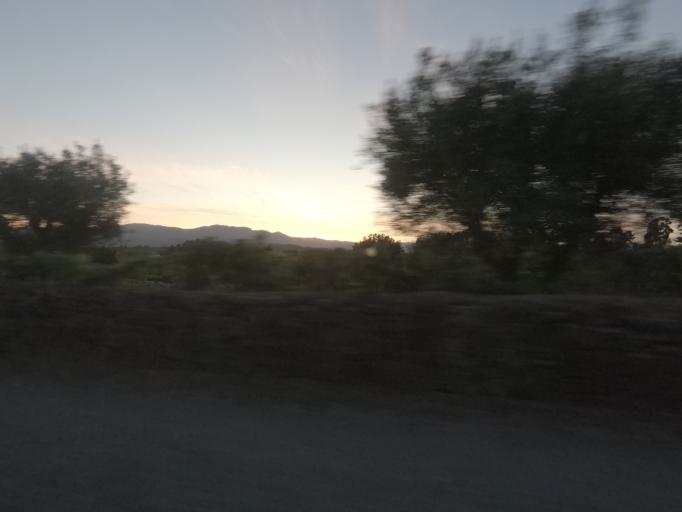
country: PT
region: Vila Real
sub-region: Peso da Regua
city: Peso da Regua
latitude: 41.2018
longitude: -7.7027
